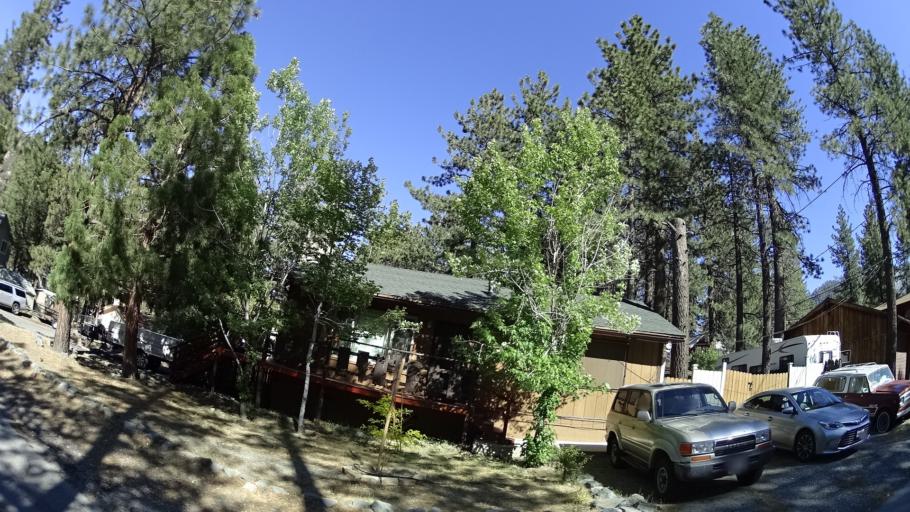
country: US
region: California
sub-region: San Bernardino County
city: Wrightwood
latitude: 34.3590
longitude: -117.6358
